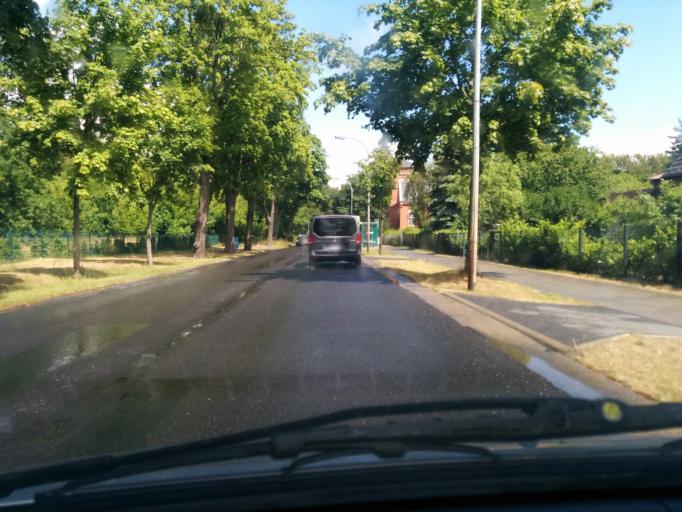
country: DE
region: Brandenburg
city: Falkensee
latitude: 52.5749
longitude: 13.1057
